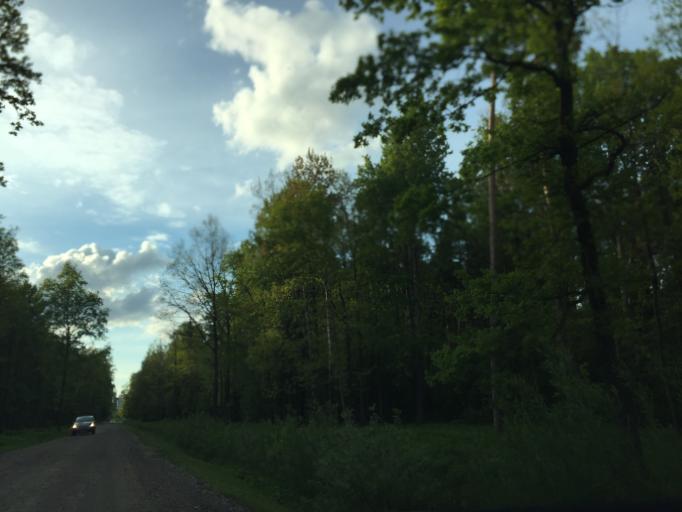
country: LV
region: Ozolnieku
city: Ozolnieki
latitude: 56.6571
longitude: 23.7792
